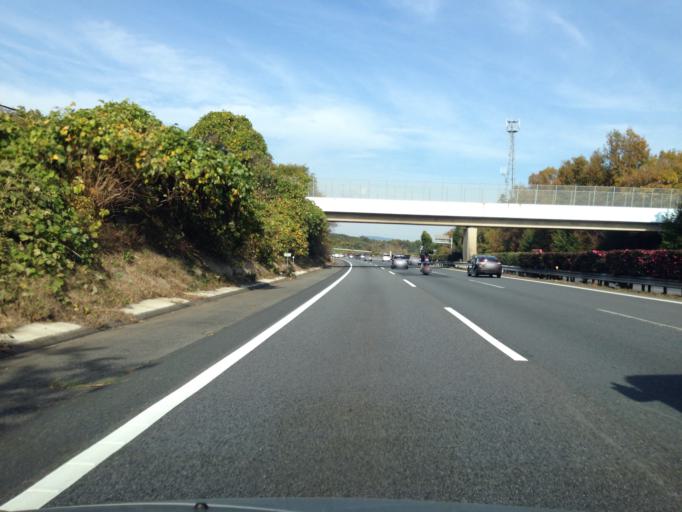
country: JP
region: Ibaraki
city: Naka
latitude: 36.0619
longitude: 140.1572
